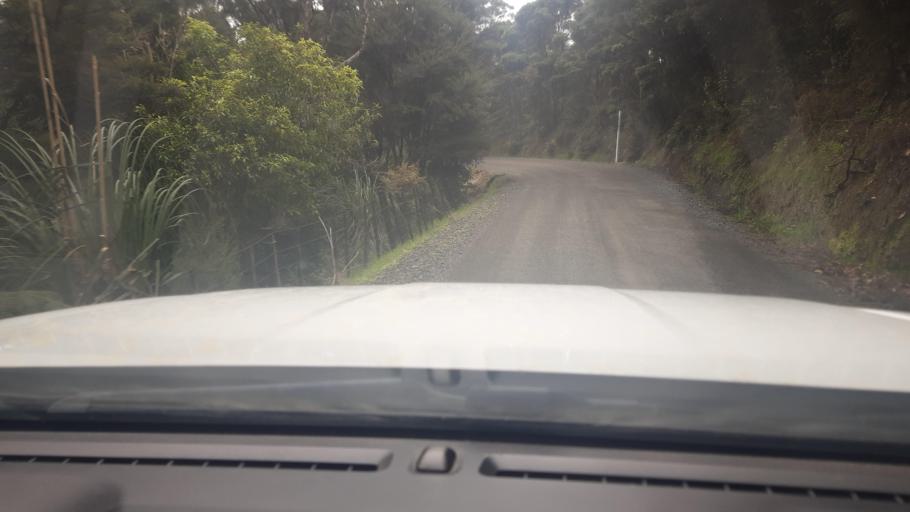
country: NZ
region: Northland
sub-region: Far North District
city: Kaitaia
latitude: -35.0680
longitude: 173.3318
